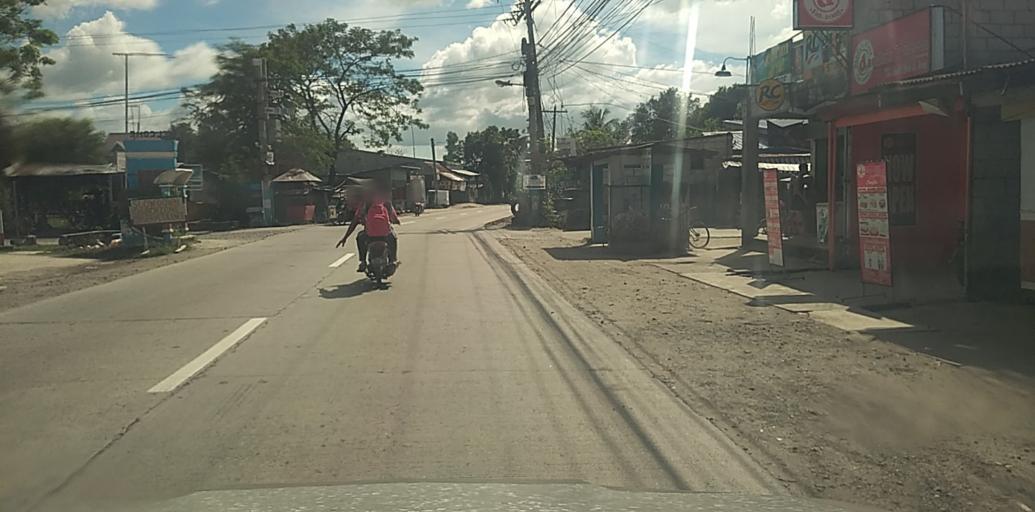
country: PH
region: Central Luzon
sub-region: Province of Pampanga
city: Buensuseso
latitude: 15.1927
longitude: 120.6735
